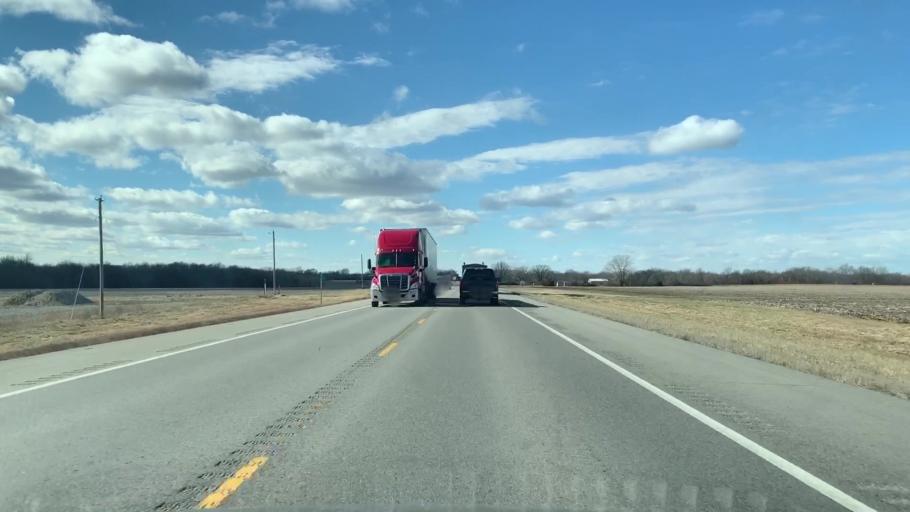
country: US
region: Kansas
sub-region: Cherokee County
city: Columbus
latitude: 37.3399
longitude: -94.8766
